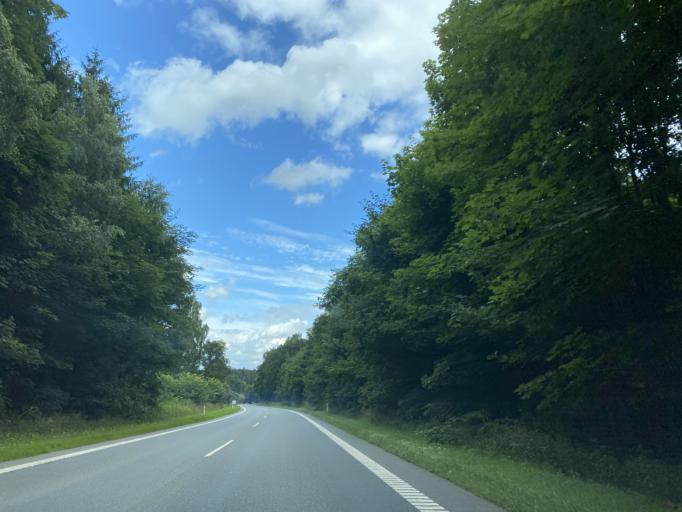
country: DK
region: Central Jutland
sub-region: Silkeborg Kommune
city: Silkeborg
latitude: 56.2611
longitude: 9.6233
